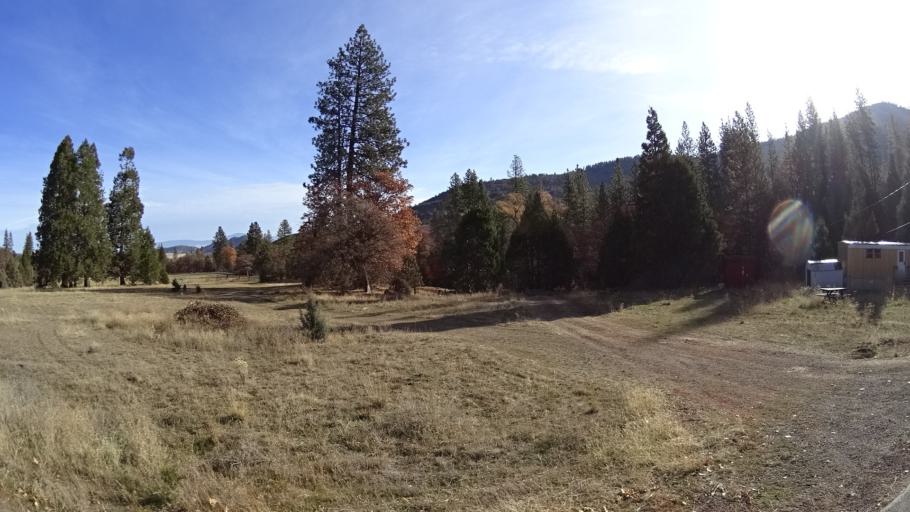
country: US
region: California
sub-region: Siskiyou County
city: Yreka
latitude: 41.6504
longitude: -122.6319
